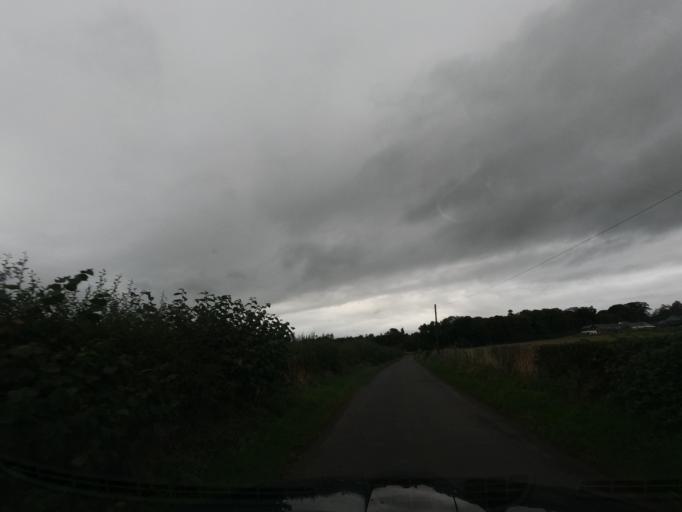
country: GB
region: England
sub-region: Northumberland
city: Ford
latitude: 55.6271
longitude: -2.0878
